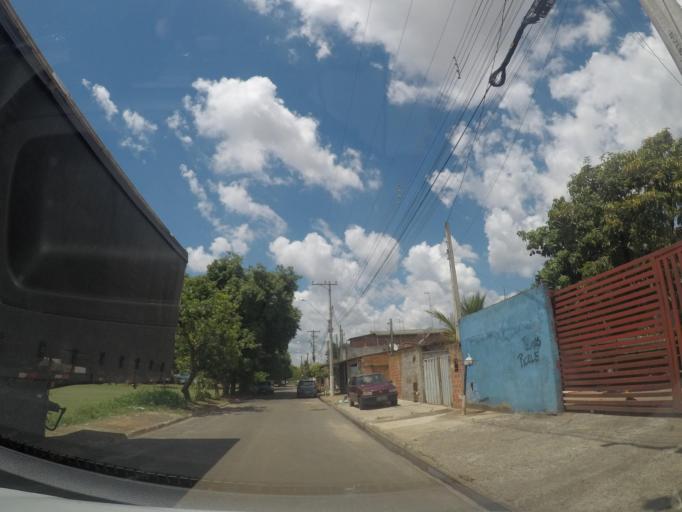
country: BR
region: Sao Paulo
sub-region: Hortolandia
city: Hortolandia
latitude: -22.8197
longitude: -47.2000
